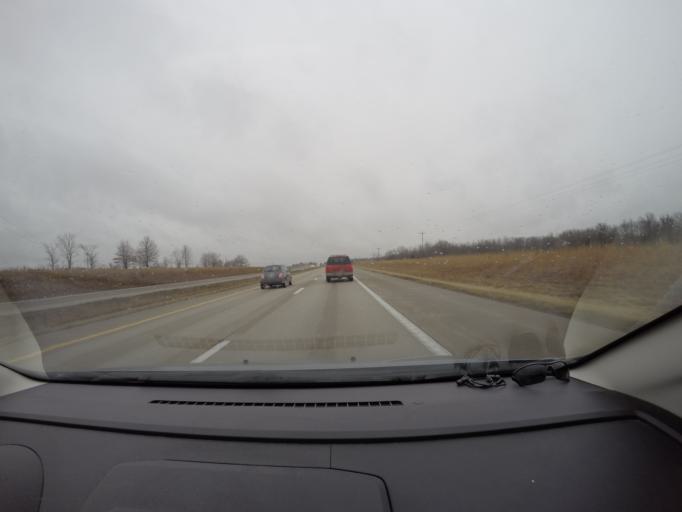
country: US
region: Missouri
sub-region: Callaway County
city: Fulton
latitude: 38.9255
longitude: -91.7758
